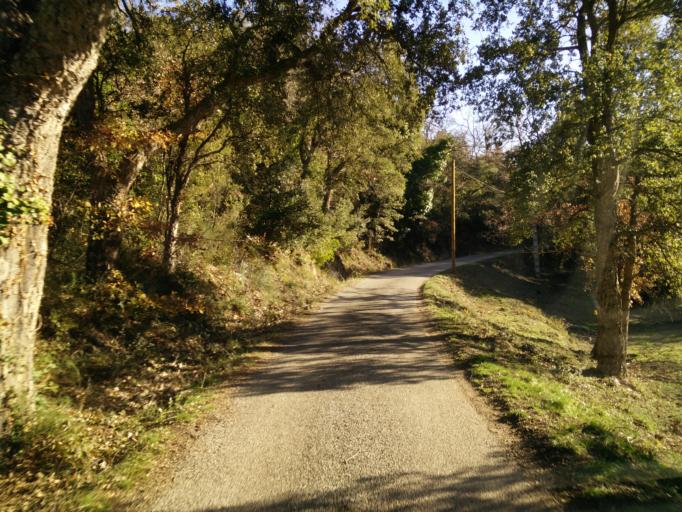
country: FR
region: Provence-Alpes-Cote d'Azur
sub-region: Departement du Var
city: Collobrieres
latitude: 43.2519
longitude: 6.3100
